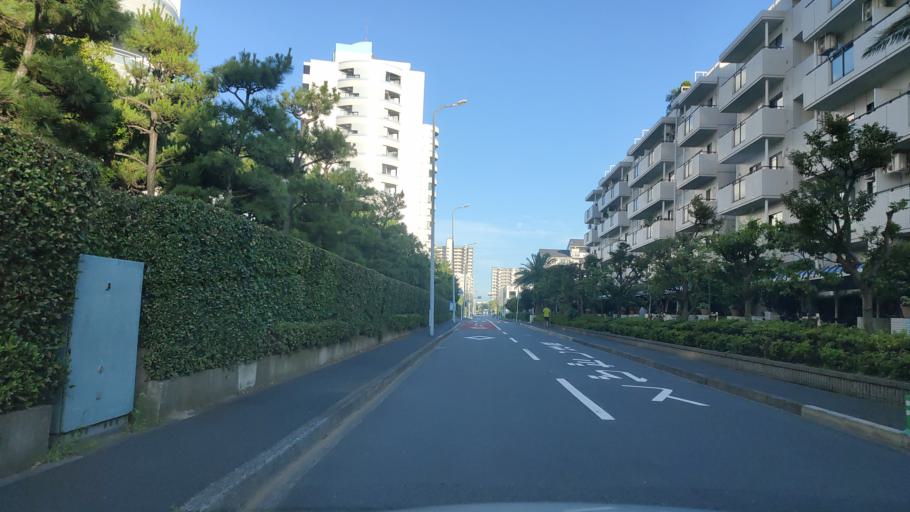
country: JP
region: Tokyo
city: Urayasu
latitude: 35.6467
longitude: 139.9229
